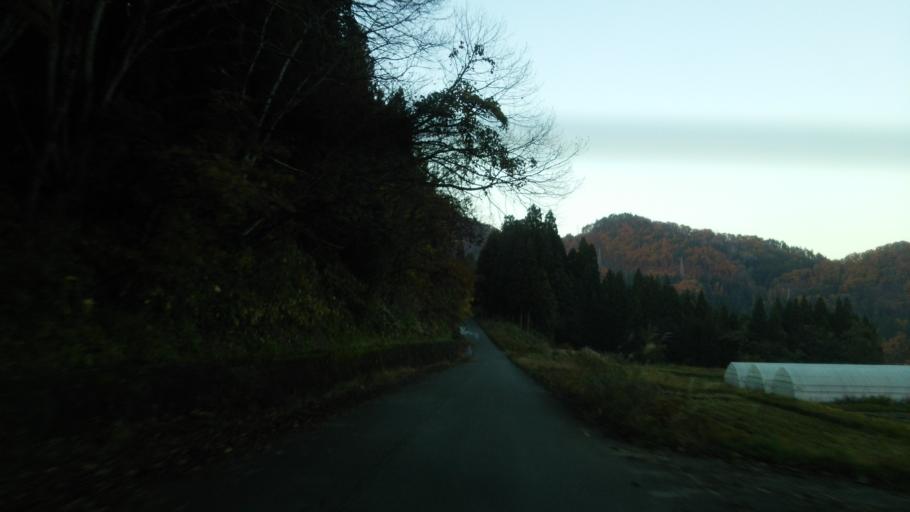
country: JP
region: Fukushima
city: Kitakata
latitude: 37.4892
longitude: 139.6637
